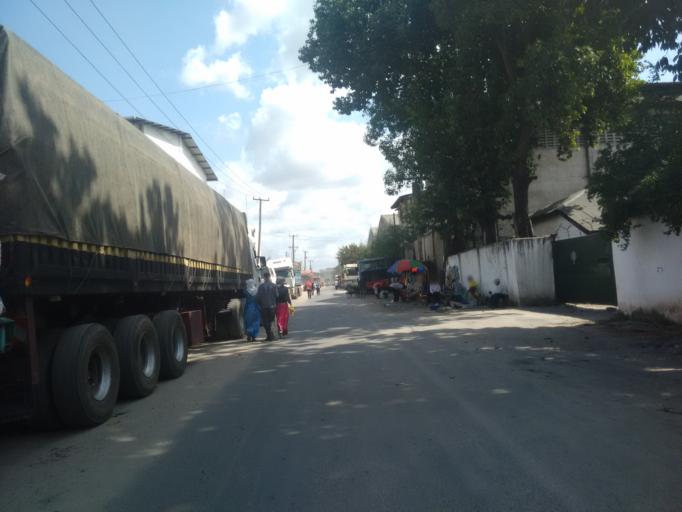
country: TZ
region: Dar es Salaam
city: Dar es Salaam
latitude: -6.8397
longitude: 39.2626
